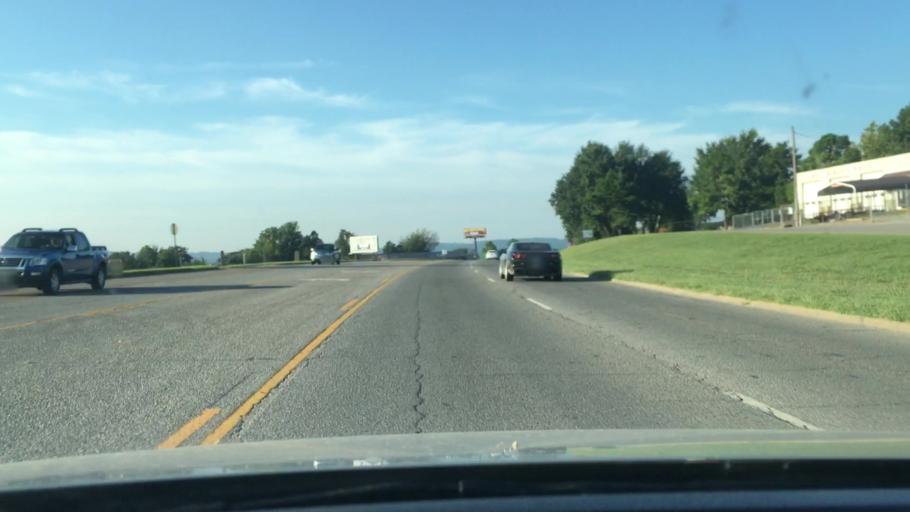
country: US
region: Oklahoma
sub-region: Cherokee County
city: Park Hill
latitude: 35.8641
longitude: -94.9763
